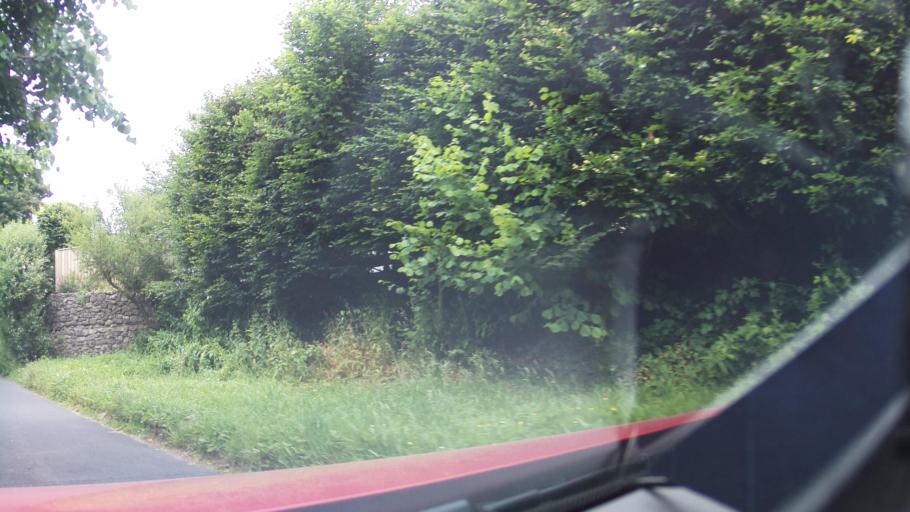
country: GB
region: England
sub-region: Devon
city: Totnes
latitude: 50.4396
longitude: -3.7074
